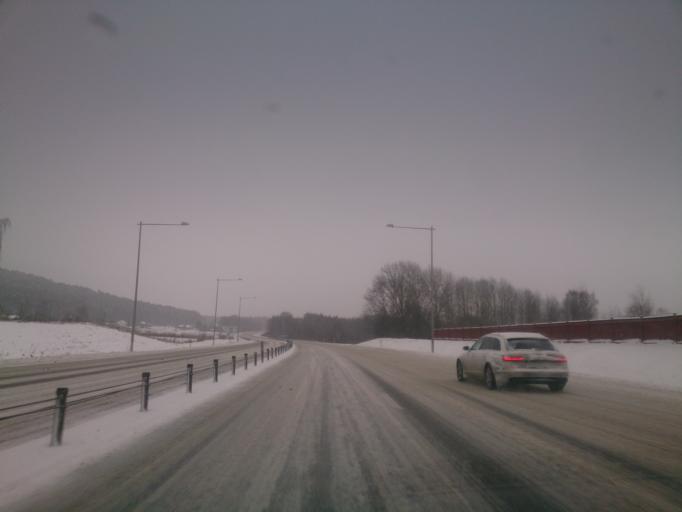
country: SE
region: OEstergoetland
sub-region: Norrkopings Kommun
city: Svartinge
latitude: 58.6468
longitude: 16.0594
